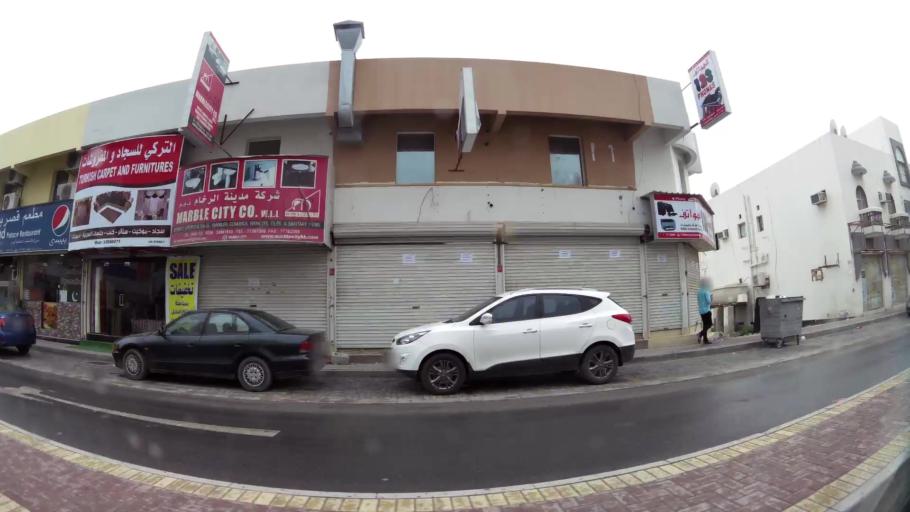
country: BH
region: Northern
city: Ar Rifa'
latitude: 26.1249
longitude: 50.5678
